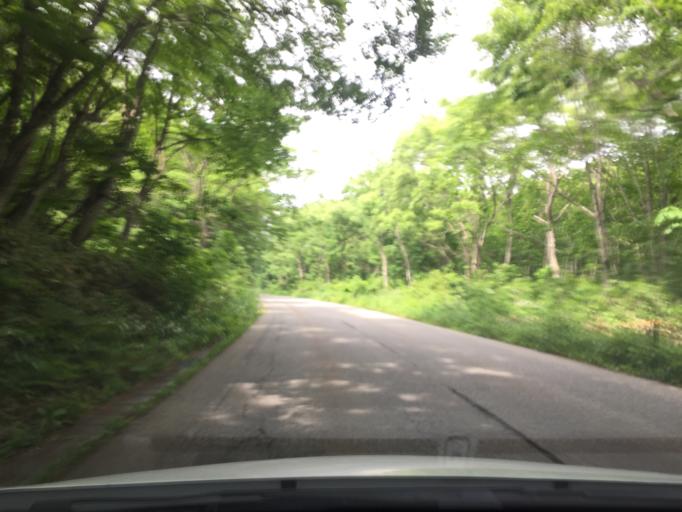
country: JP
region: Fukushima
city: Inawashiro
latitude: 37.6459
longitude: 140.0353
